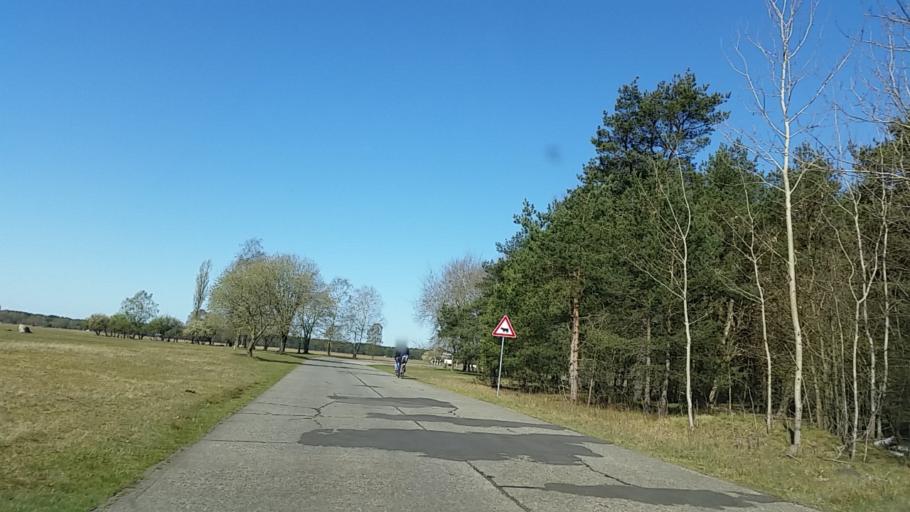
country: DE
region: Lower Saxony
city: Schneverdingen
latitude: 53.1518
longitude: 9.8323
